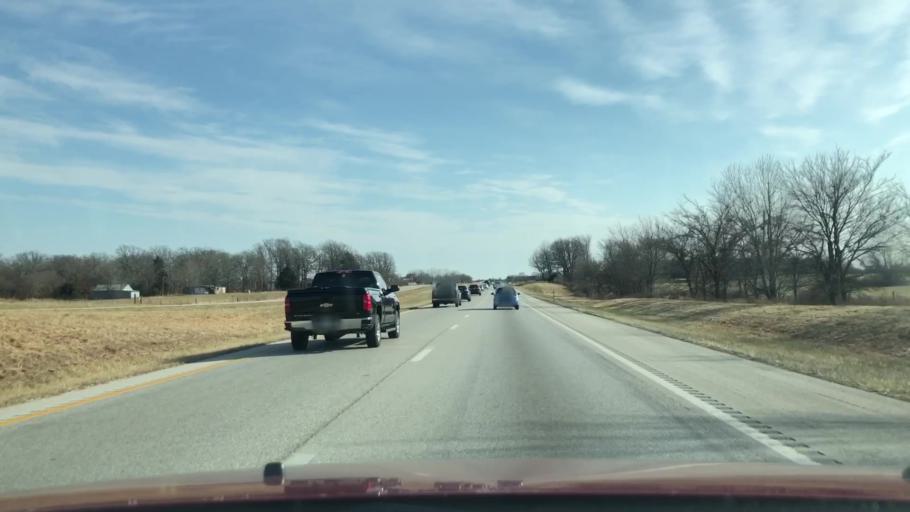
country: US
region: Missouri
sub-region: Webster County
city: Rogersville
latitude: 37.1185
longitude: -93.1138
